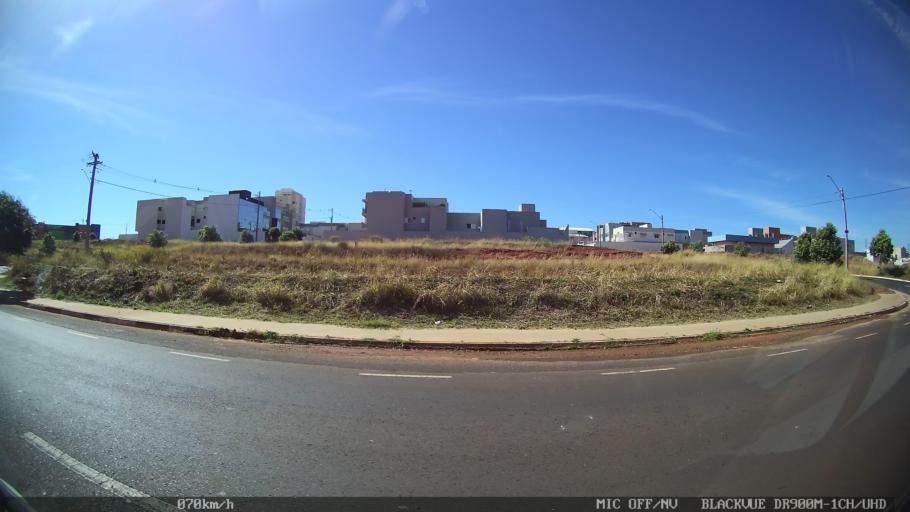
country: BR
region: Sao Paulo
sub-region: Franca
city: Franca
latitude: -20.5353
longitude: -47.3758
